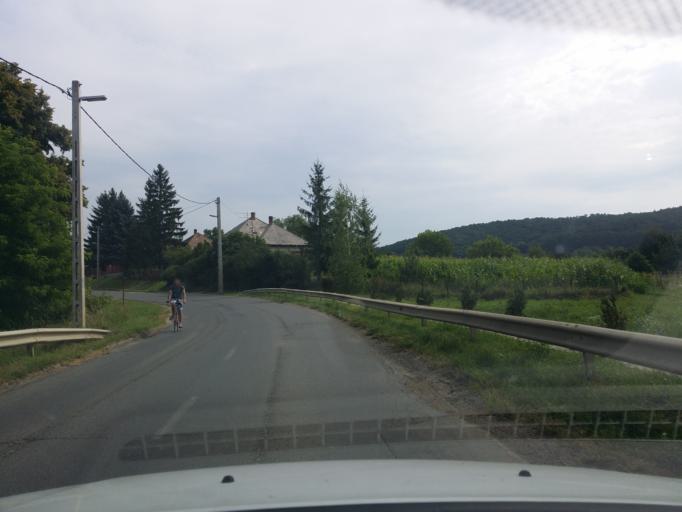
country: HU
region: Pest
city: Acsa
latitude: 47.7982
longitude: 19.3832
